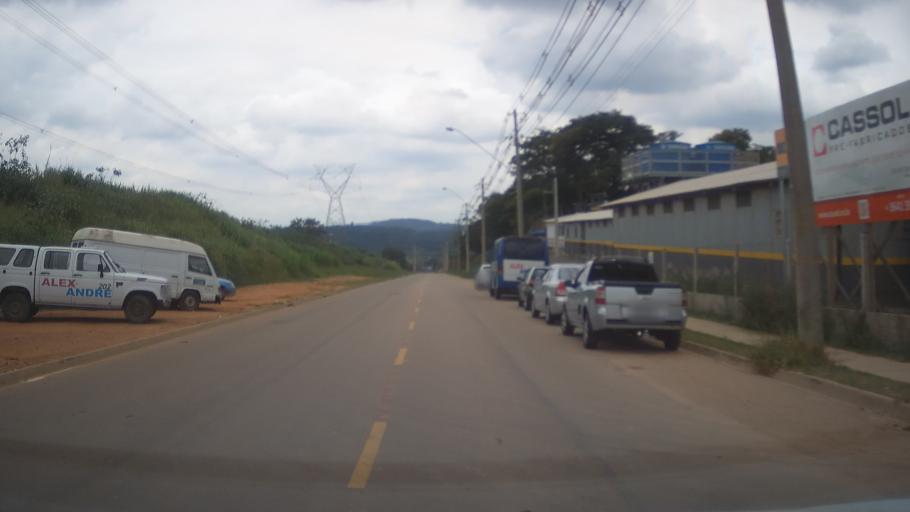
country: BR
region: Sao Paulo
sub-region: Itupeva
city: Itupeva
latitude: -23.1496
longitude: -47.0012
